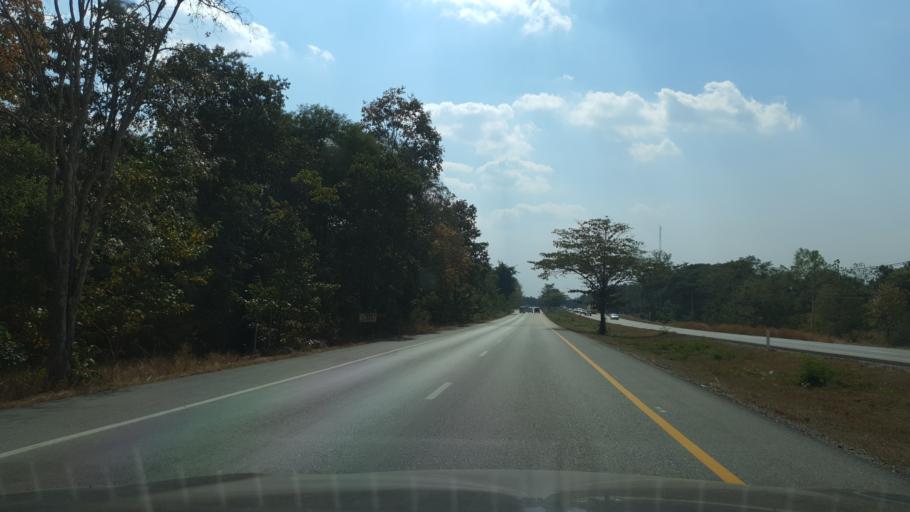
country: TH
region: Lampang
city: Mae Phrik
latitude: 17.3127
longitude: 99.1496
